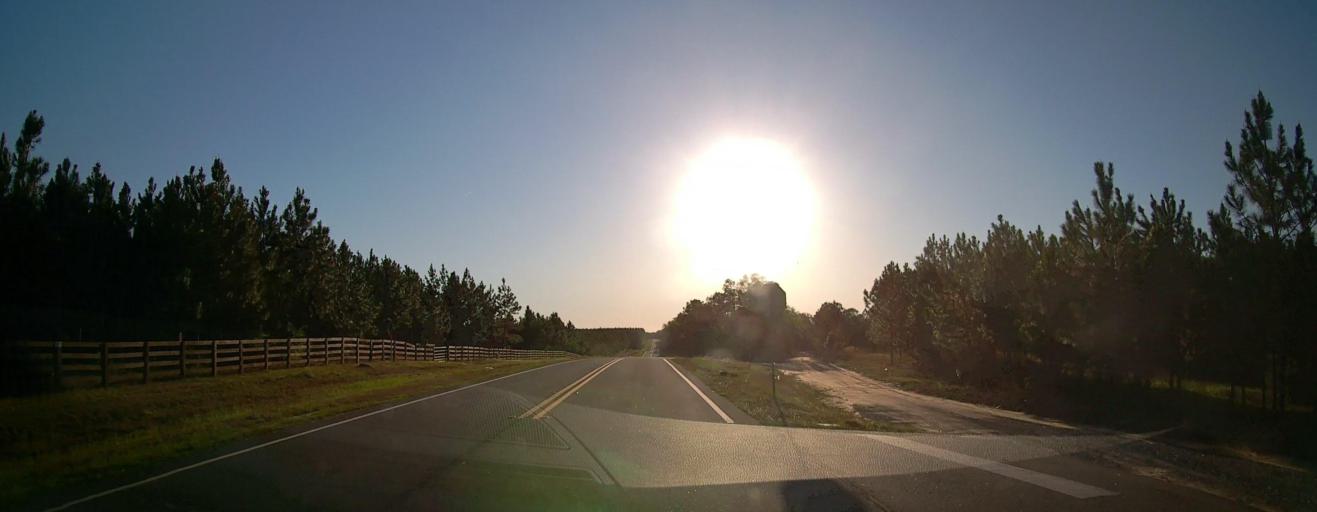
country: US
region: Georgia
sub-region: Wilcox County
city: Abbeville
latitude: 31.9885
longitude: -83.3307
